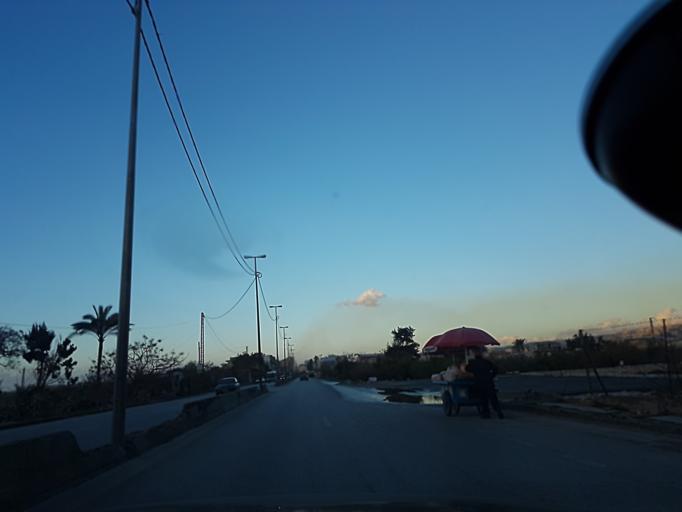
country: LB
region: Liban-Sud
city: Sidon
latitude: 33.5441
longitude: 35.3662
